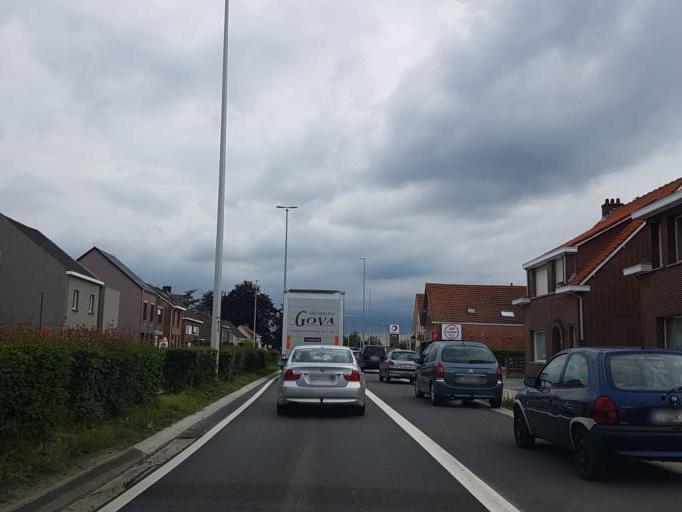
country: BE
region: Flanders
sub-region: Provincie Antwerpen
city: Zandhoven
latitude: 51.2012
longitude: 4.6444
